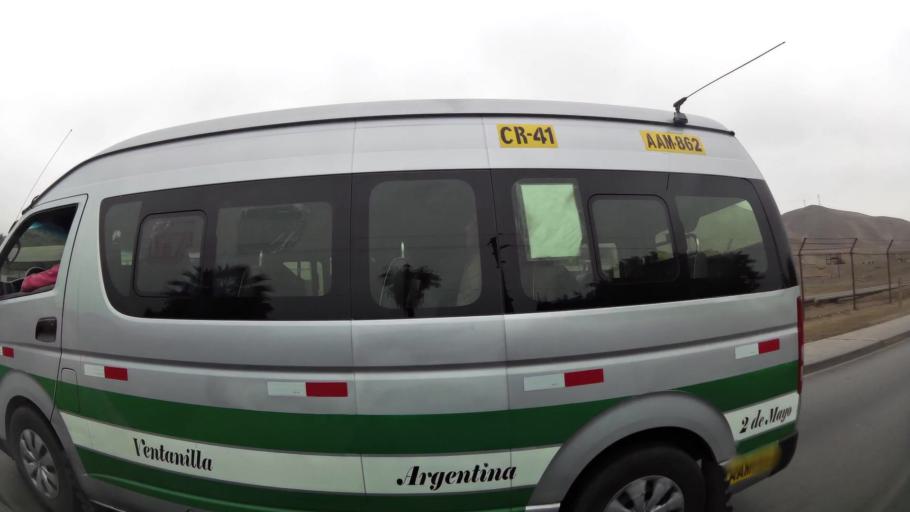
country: PE
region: Lima
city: Ventanilla
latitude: -11.9210
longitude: -77.1289
